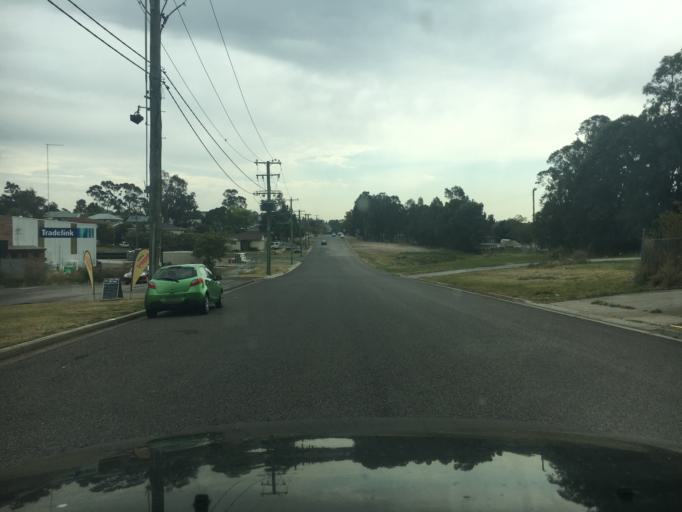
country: AU
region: New South Wales
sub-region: Maitland Municipality
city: East Maitland
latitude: -32.7601
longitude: 151.5994
